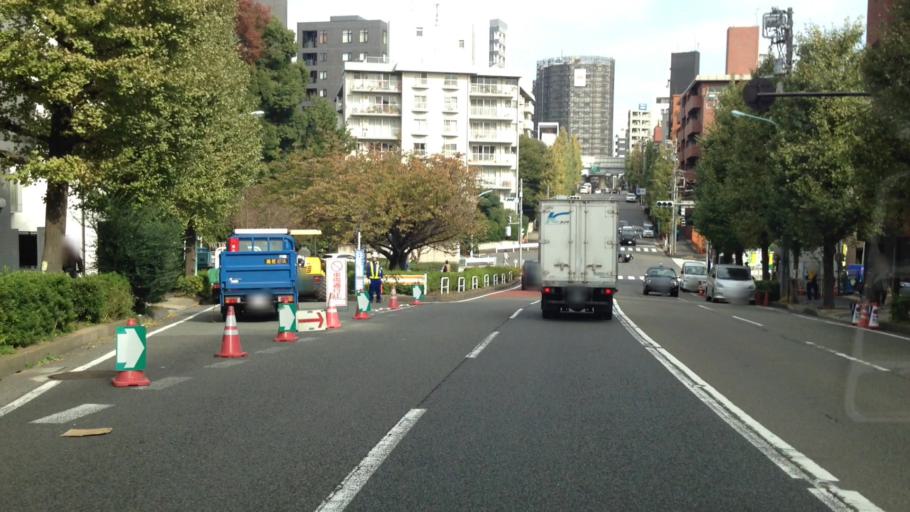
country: JP
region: Tokyo
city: Tokyo
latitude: 35.6565
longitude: 139.7140
